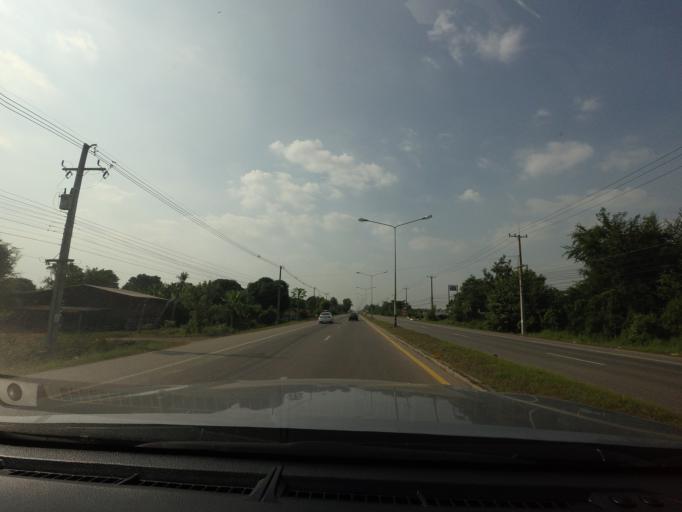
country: TH
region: Sukhothai
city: Kong Krailat
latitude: 17.0112
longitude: 99.9204
